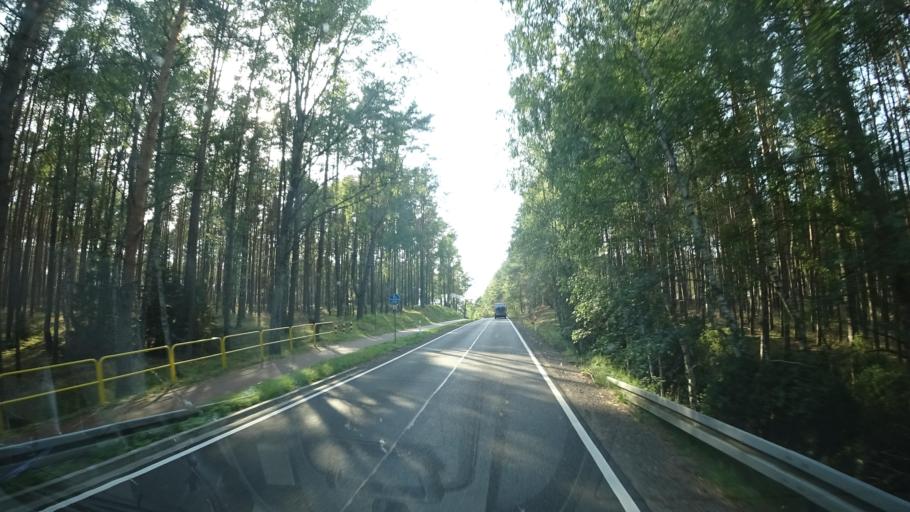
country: PL
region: Pomeranian Voivodeship
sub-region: Powiat chojnicki
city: Chojnice
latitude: 53.8539
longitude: 17.5613
